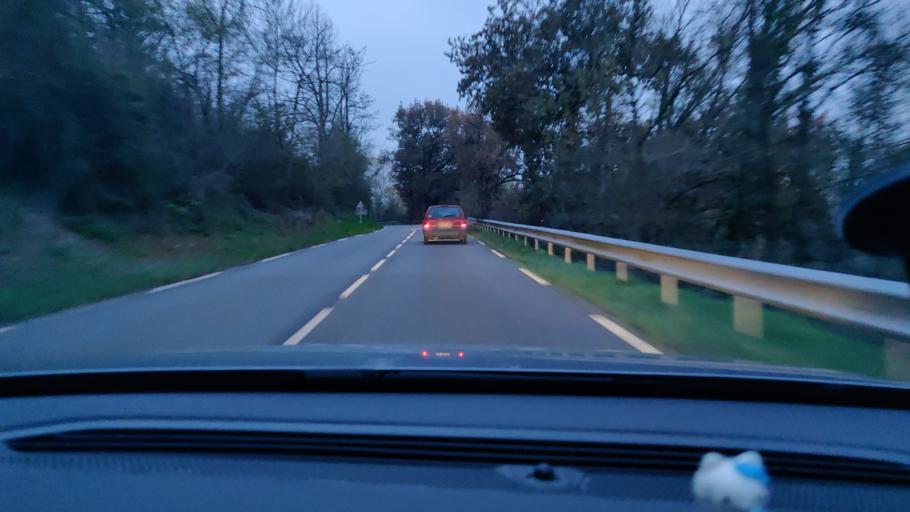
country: FR
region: Midi-Pyrenees
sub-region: Departement de la Haute-Garonne
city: Vieille-Toulouse
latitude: 43.5386
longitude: 1.4335
